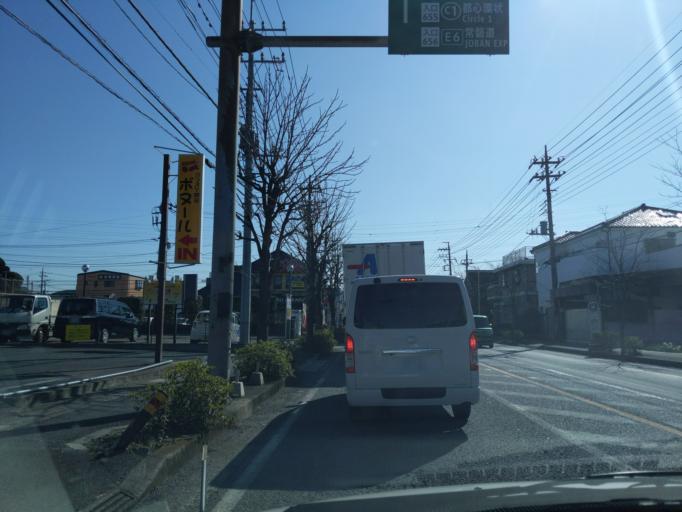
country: JP
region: Saitama
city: Yashio-shi
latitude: 35.8211
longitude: 139.8257
